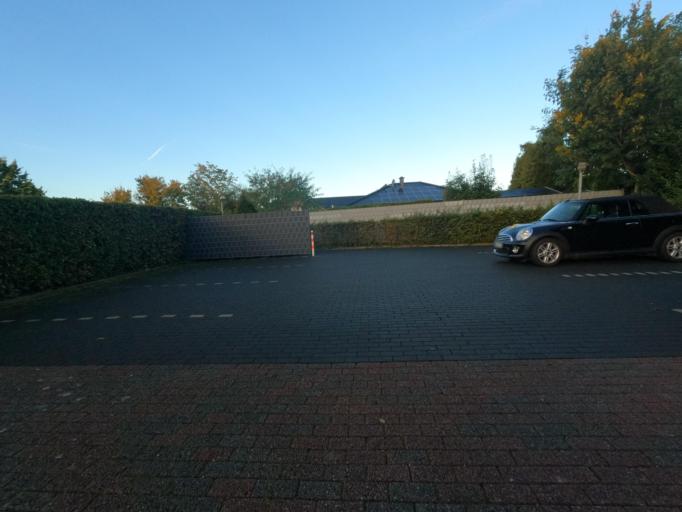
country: DE
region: North Rhine-Westphalia
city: Erkelenz
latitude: 51.0647
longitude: 6.3258
